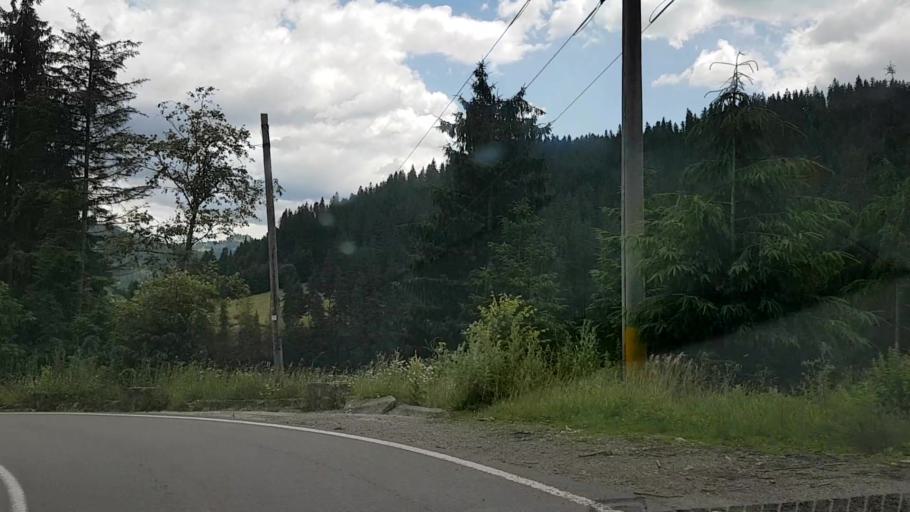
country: RO
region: Suceava
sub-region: Comuna Crucea
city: Crucea
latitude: 47.3621
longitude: 25.5919
